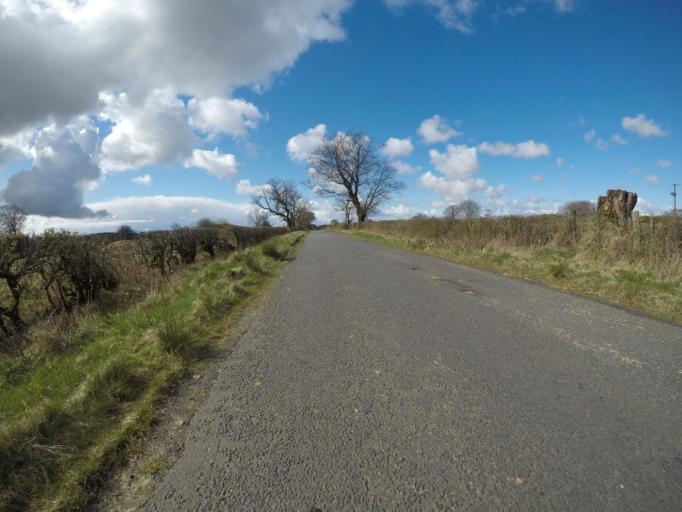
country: GB
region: Scotland
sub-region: North Ayrshire
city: Kilbirnie
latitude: 55.7182
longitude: -4.6779
